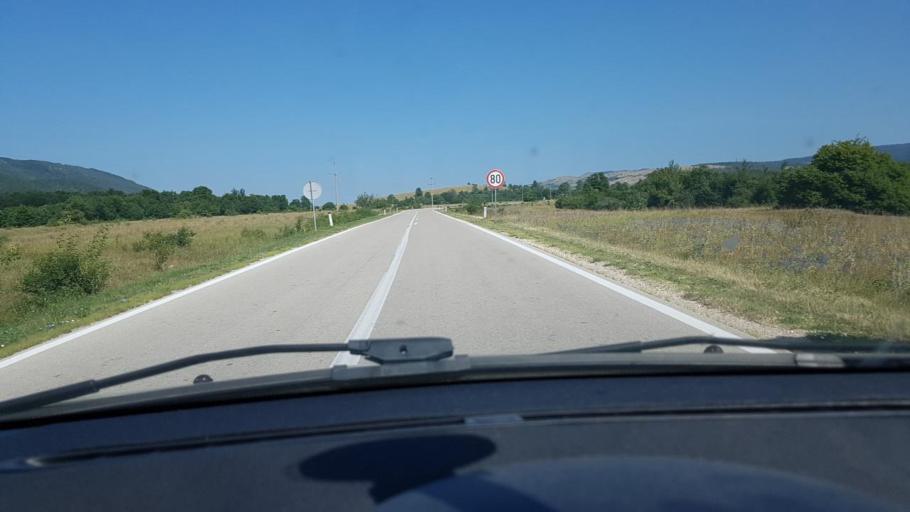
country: BA
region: Federation of Bosnia and Herzegovina
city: Bosansko Grahovo
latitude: 44.0988
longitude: 16.5542
